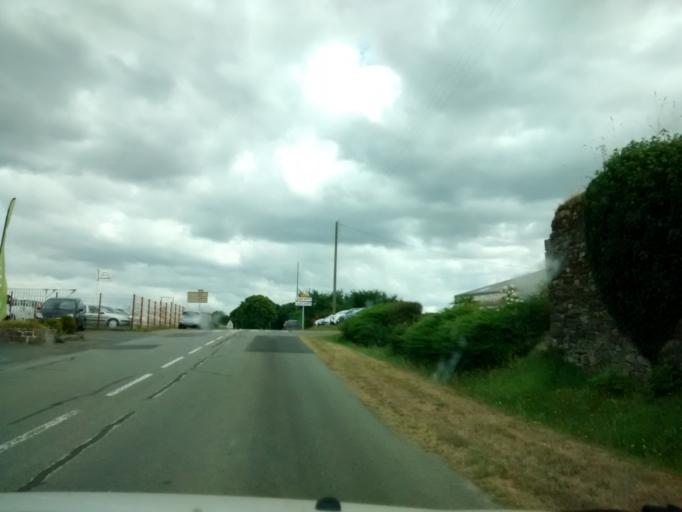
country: FR
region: Brittany
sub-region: Departement du Finistere
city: Plouneventer
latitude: 48.5599
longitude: -4.2580
